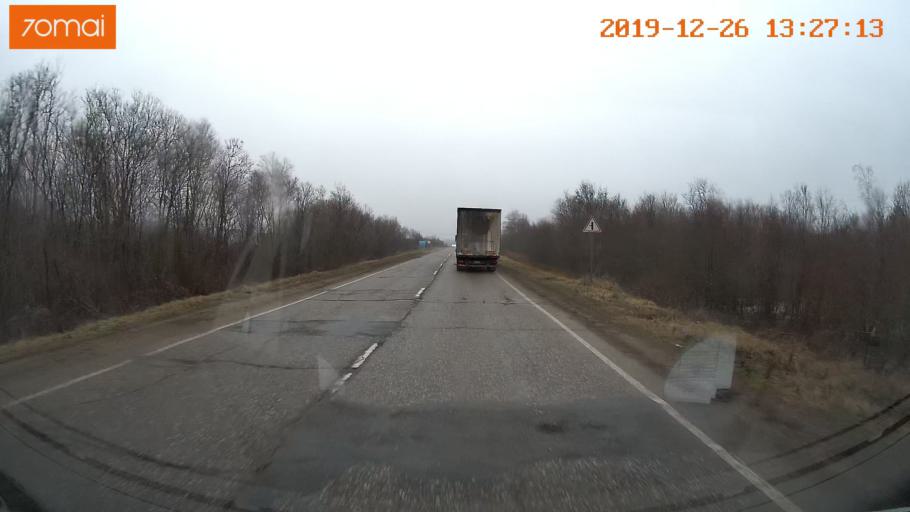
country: RU
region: Vologda
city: Cherepovets
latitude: 58.8551
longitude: 38.2380
